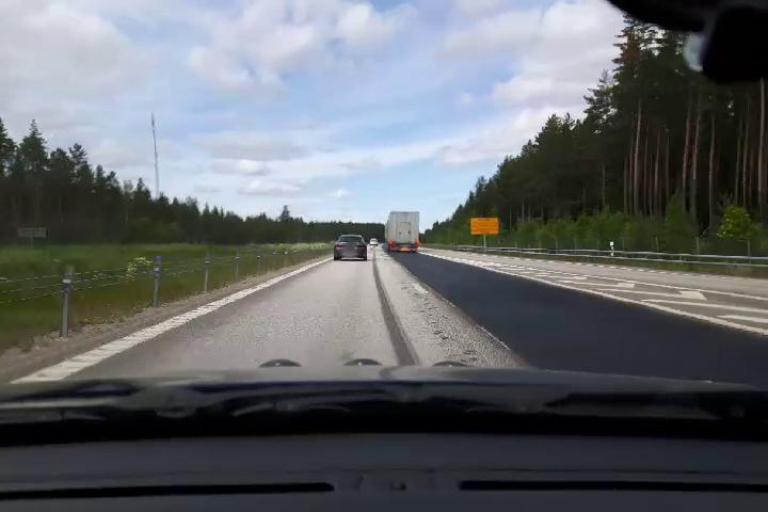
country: SE
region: Uppsala
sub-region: Alvkarleby Kommun
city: AElvkarleby
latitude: 60.4414
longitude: 17.4197
